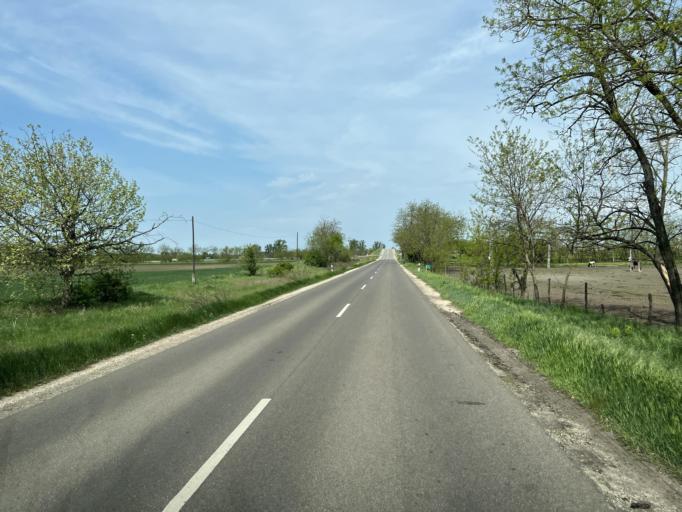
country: HU
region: Pest
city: Abony
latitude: 47.2126
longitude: 19.9835
